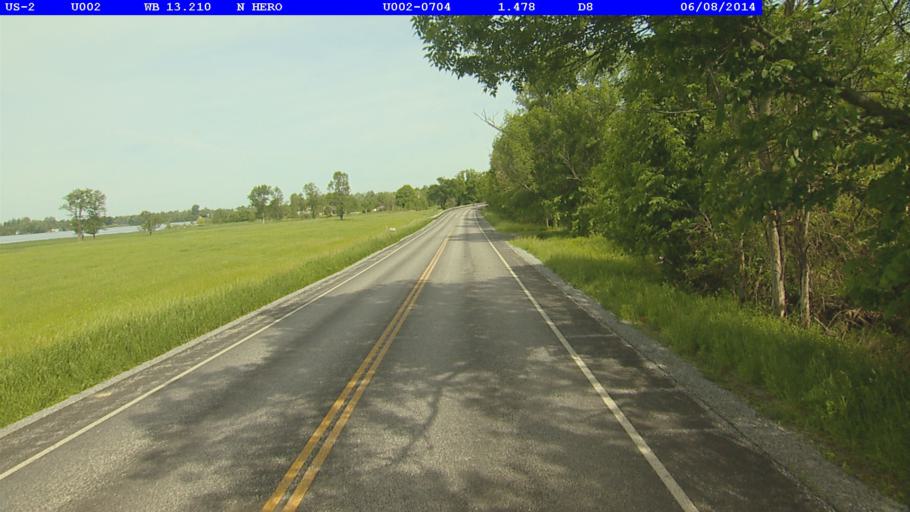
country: US
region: Vermont
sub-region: Grand Isle County
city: North Hero
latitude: 44.8659
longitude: -73.2671
